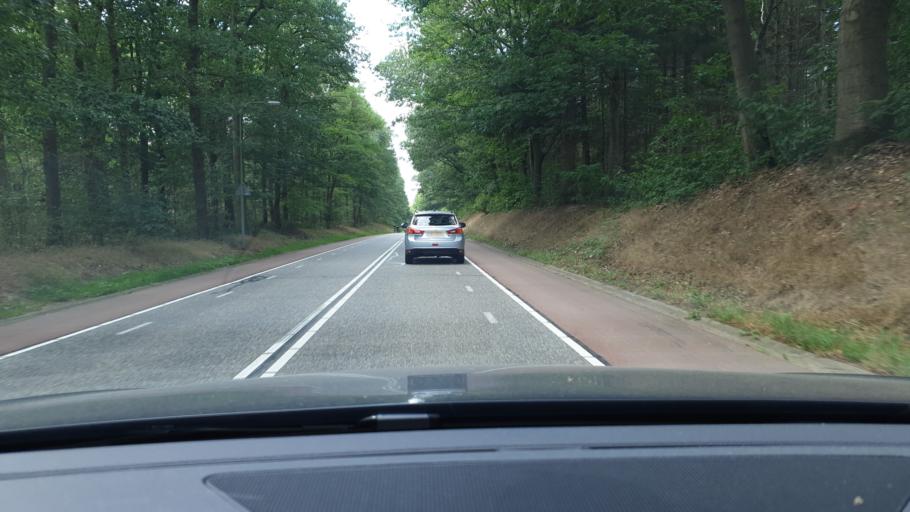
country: NL
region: North Brabant
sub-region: Gemeente Cuijk
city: Cuijk
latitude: 51.7579
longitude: 5.8937
